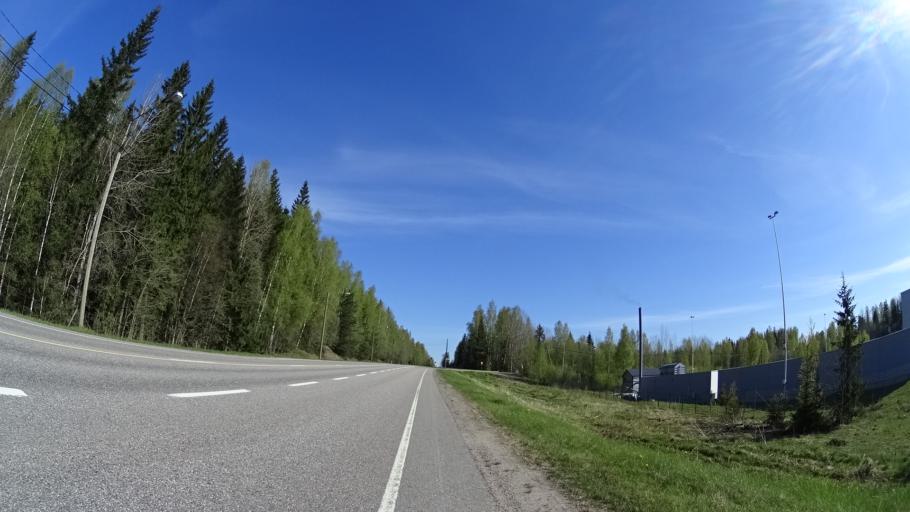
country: FI
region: Uusimaa
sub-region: Helsinki
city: Nurmijaervi
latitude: 60.3712
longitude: 24.8054
